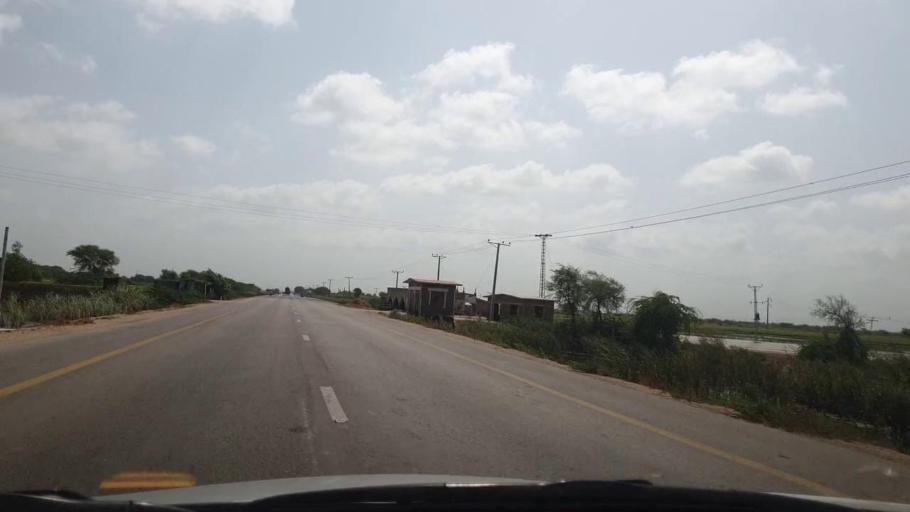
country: PK
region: Sindh
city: Talhar
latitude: 24.9029
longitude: 68.7576
